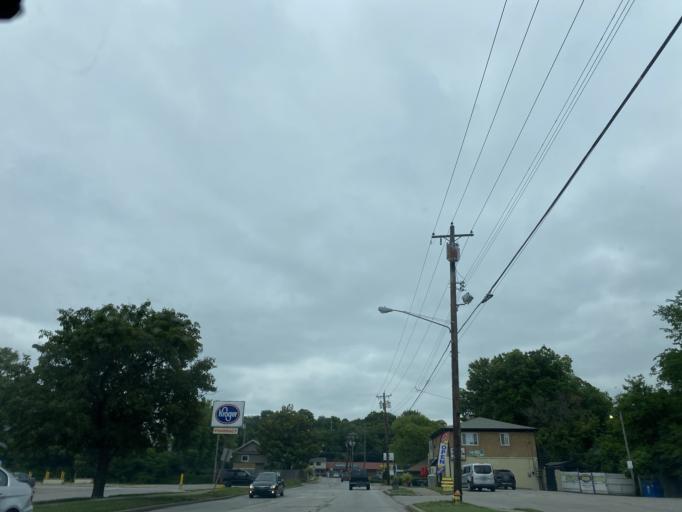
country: US
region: Kentucky
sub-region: Campbell County
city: Bellevue
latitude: 39.0983
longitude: -84.4813
